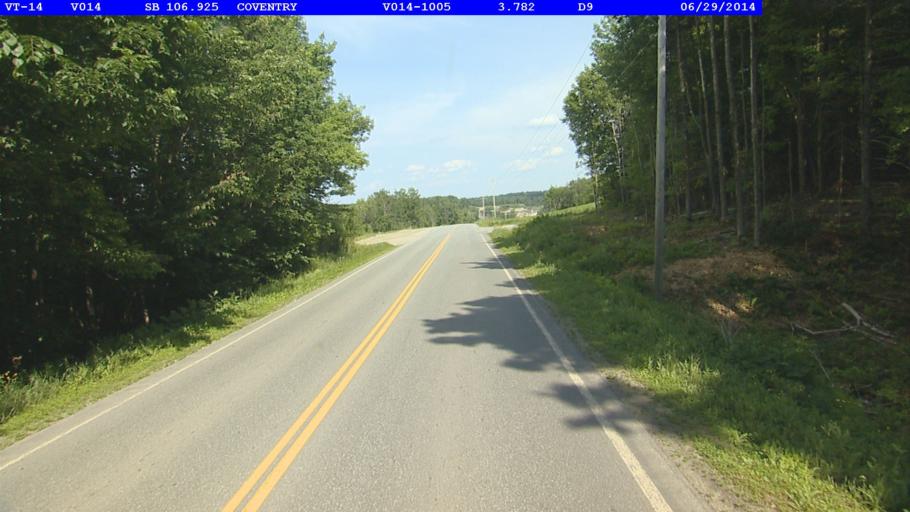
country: US
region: Vermont
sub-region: Orleans County
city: Newport
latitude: 44.9118
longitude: -72.2721
